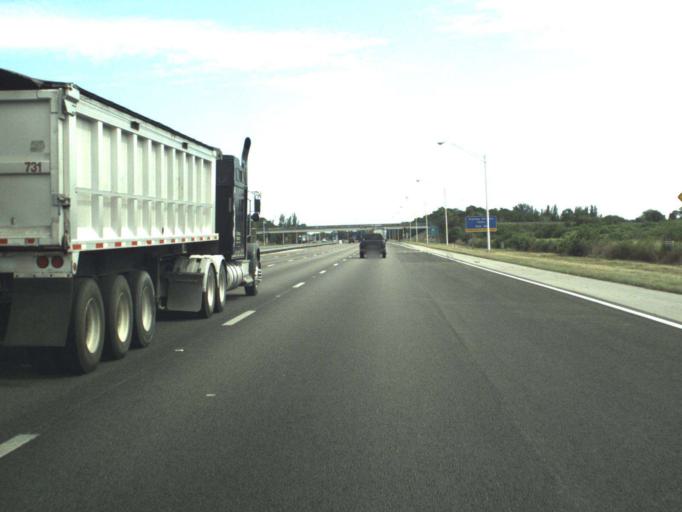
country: US
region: Florida
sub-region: Saint Lucie County
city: Fort Pierce South
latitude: 27.4253
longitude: -80.3882
